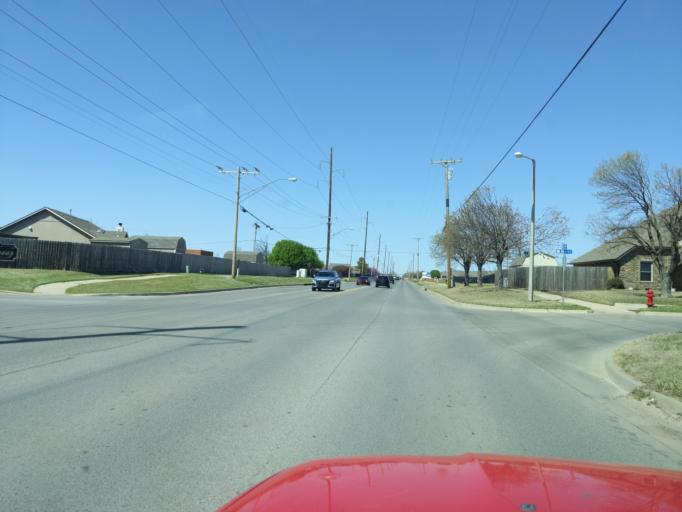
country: US
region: Oklahoma
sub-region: Cleveland County
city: Moore
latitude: 35.3263
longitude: -97.5120
